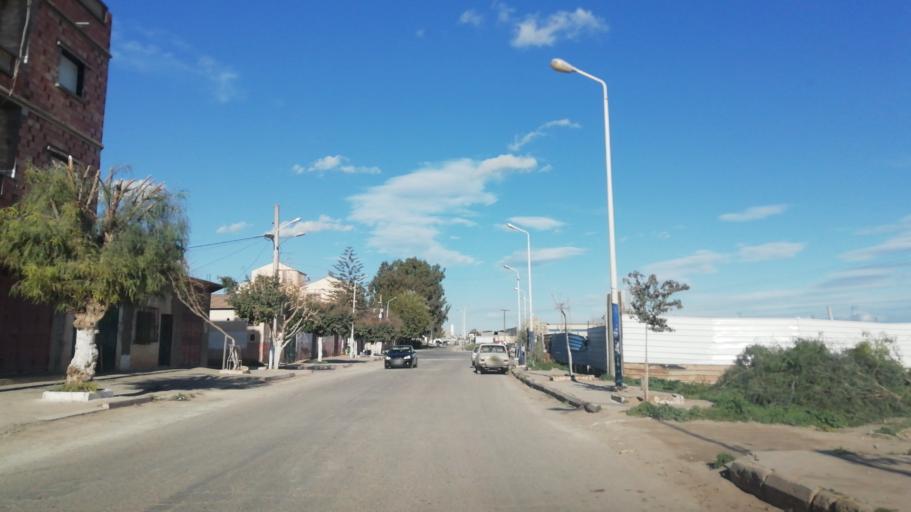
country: DZ
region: Oran
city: Sidi ech Chahmi
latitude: 35.6366
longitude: -0.5497
